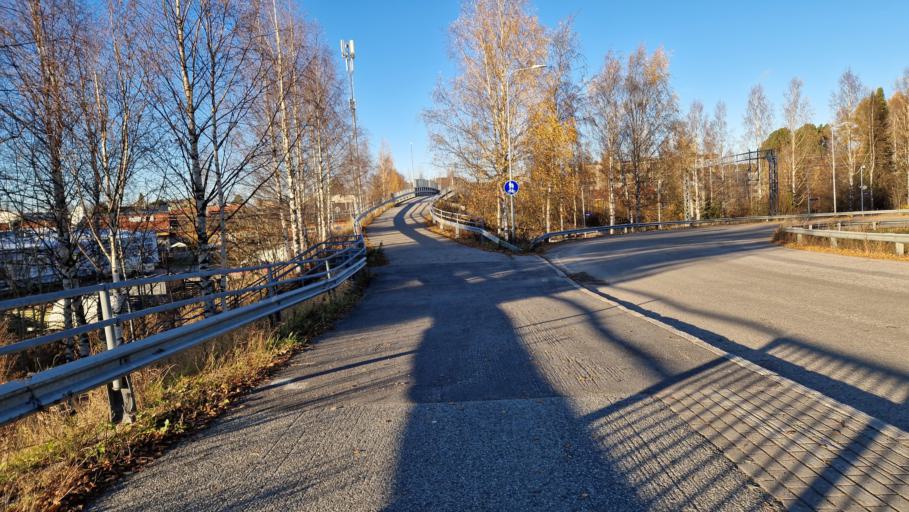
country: FI
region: Kainuu
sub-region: Kajaani
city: Kajaani
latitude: 64.2188
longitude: 27.7347
